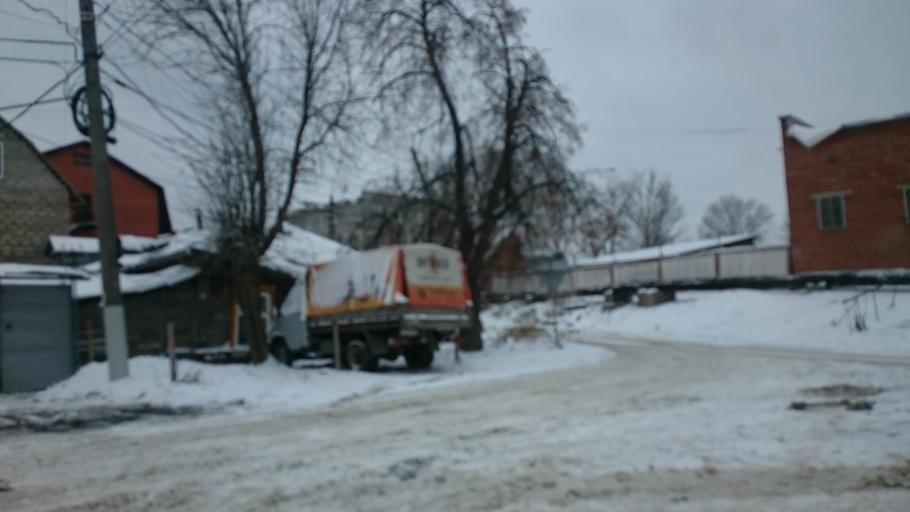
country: RU
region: Tula
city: Tula
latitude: 54.1997
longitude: 37.6287
